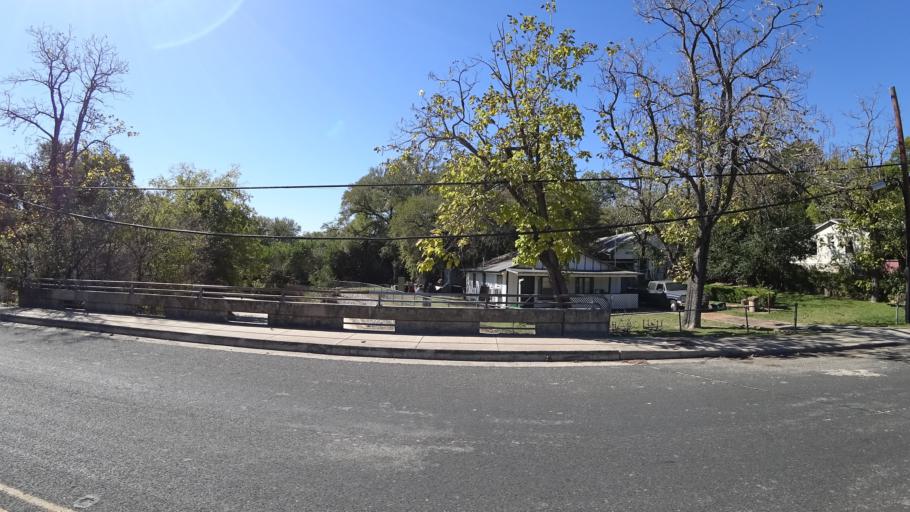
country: US
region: Texas
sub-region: Travis County
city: Austin
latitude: 30.2835
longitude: -97.6782
